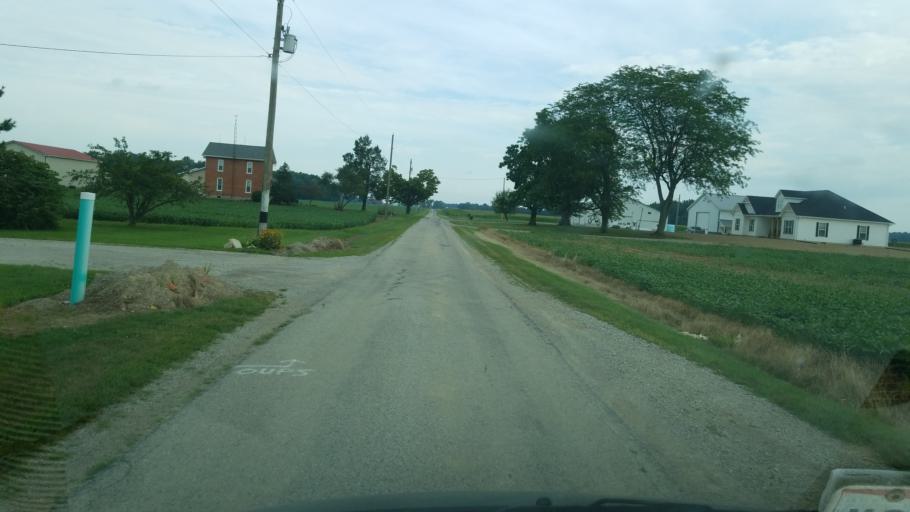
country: US
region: Ohio
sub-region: Crawford County
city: Bucyrus
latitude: 40.9733
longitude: -83.0551
